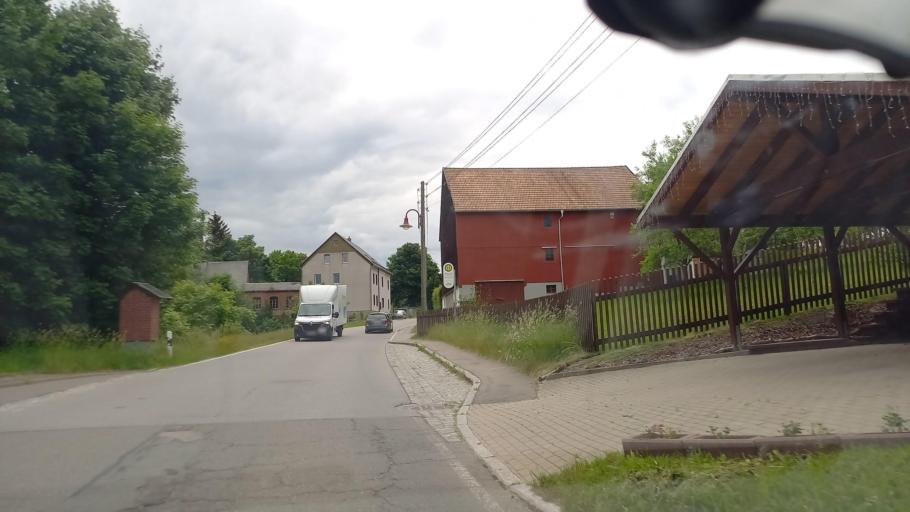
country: DE
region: Saxony
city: Stutzengrun
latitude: 50.5541
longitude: 12.5178
